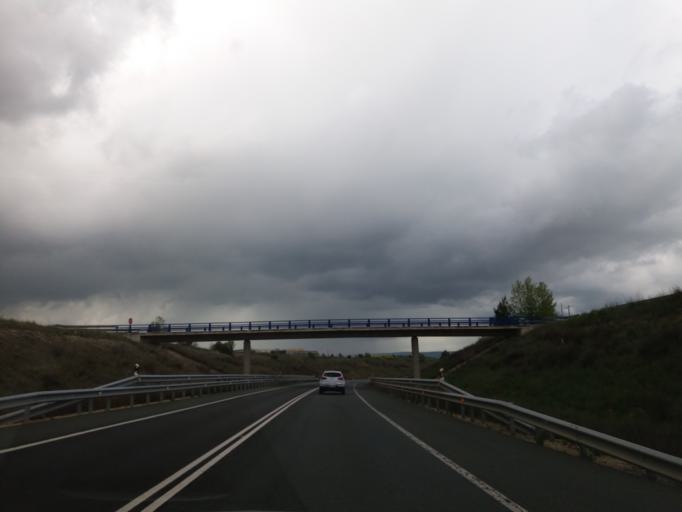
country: ES
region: La Rioja
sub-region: Provincia de La Rioja
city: Zarraton
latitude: 42.5437
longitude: -2.8793
